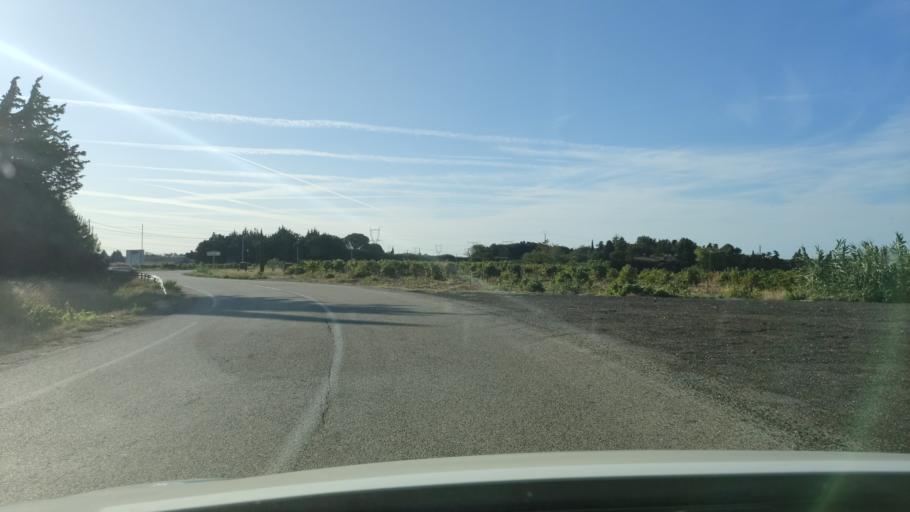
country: FR
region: Languedoc-Roussillon
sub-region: Departement du Gard
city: Saze
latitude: 43.9550
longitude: 4.6548
